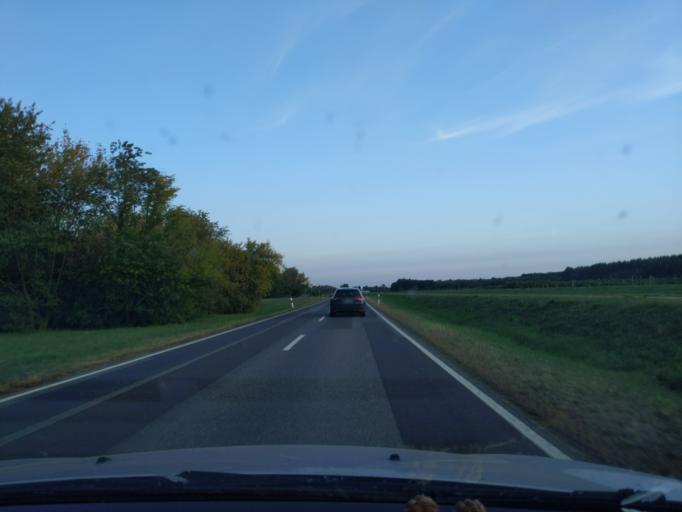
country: DE
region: Saxony
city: Hoyerswerda
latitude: 51.4756
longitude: 14.1979
